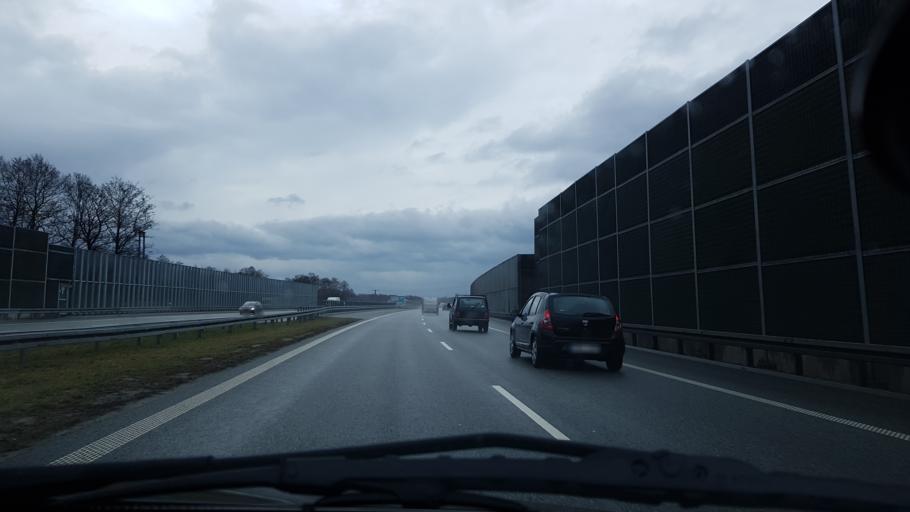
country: PL
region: Silesian Voivodeship
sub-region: Powiat bielski
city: Wilkowice
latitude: 49.7572
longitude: 19.0866
